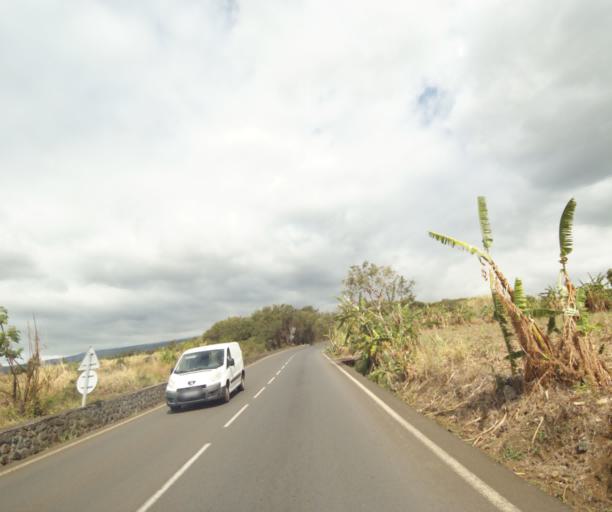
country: RE
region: Reunion
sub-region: Reunion
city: Saint-Paul
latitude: -21.0308
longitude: 55.2861
